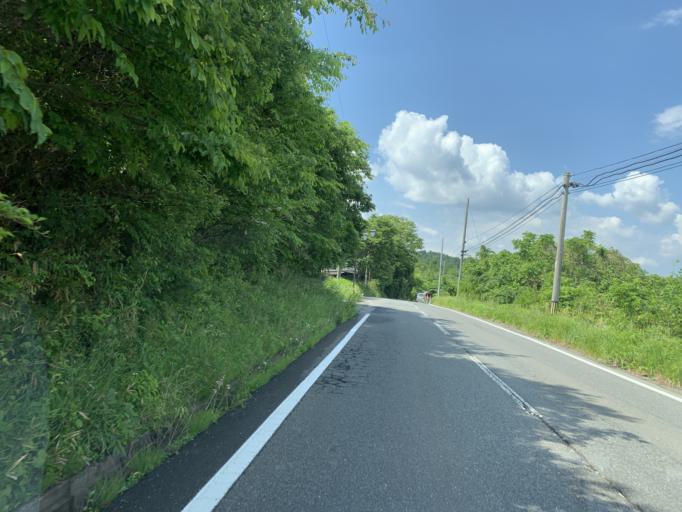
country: JP
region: Miyagi
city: Furukawa
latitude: 38.7264
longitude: 140.9521
